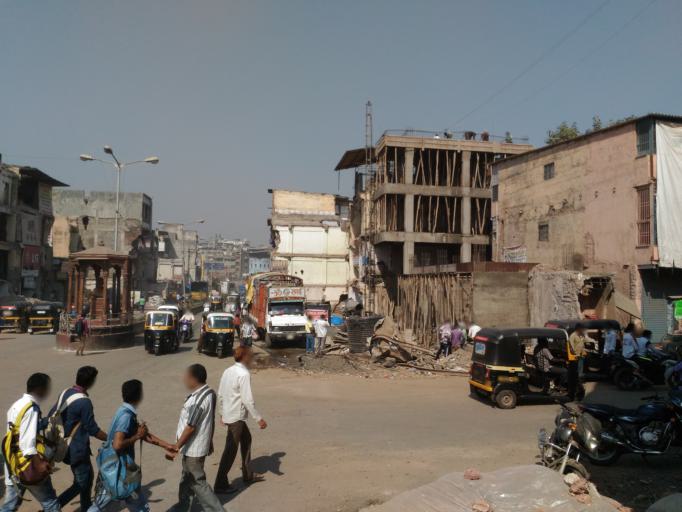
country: IN
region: Maharashtra
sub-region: Thane
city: Ulhasnagar
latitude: 19.2284
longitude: 73.1639
